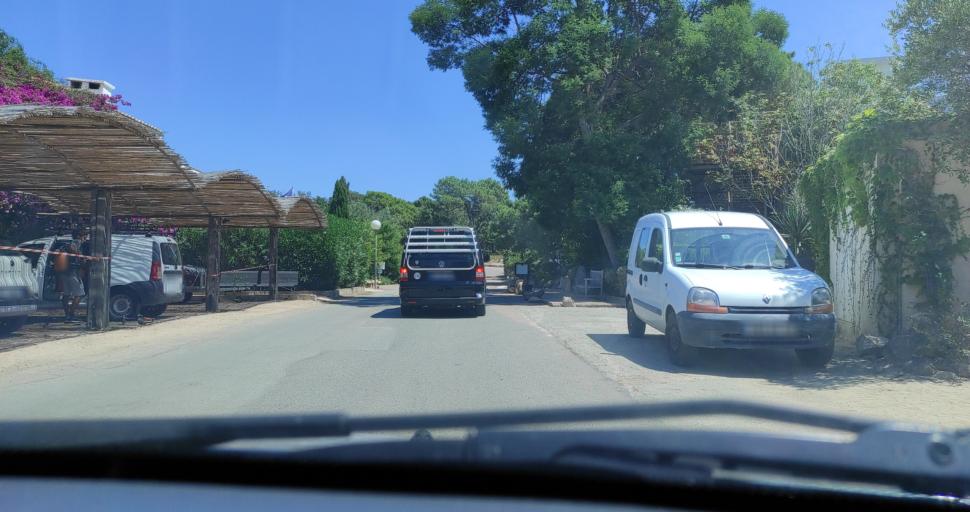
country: FR
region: Corsica
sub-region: Departement de la Corse-du-Sud
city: Porto-Vecchio
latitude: 41.6222
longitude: 9.3383
